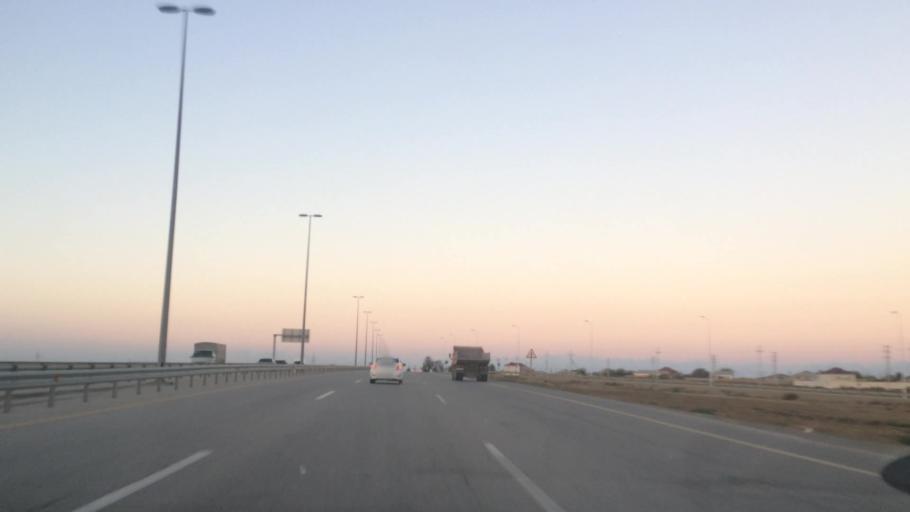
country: AZ
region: Baki
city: Qobustan
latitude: 39.9822
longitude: 49.4240
